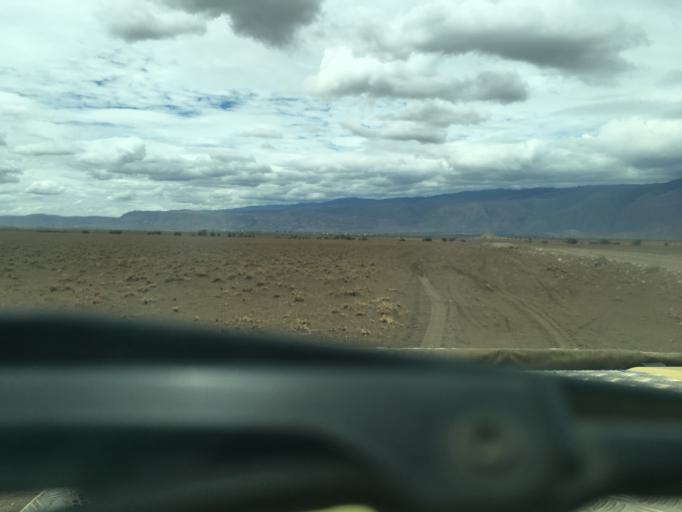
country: TZ
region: Arusha
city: Mto wa Mbu
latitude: -2.9491
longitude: 36.0397
